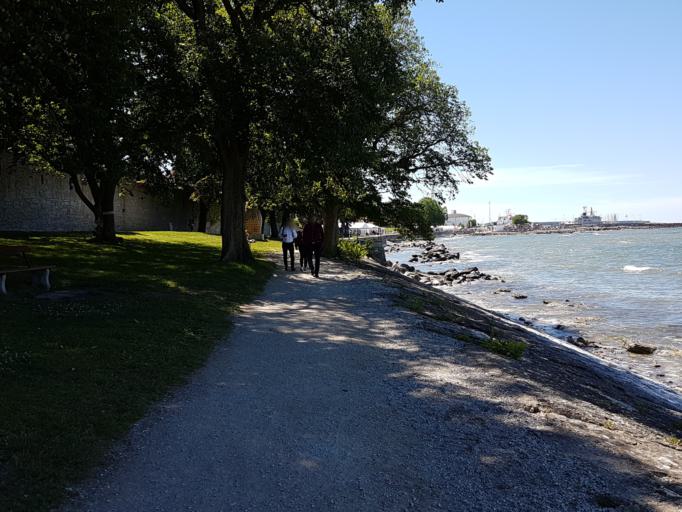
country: SE
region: Gotland
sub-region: Gotland
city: Visby
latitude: 57.6441
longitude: 18.2927
